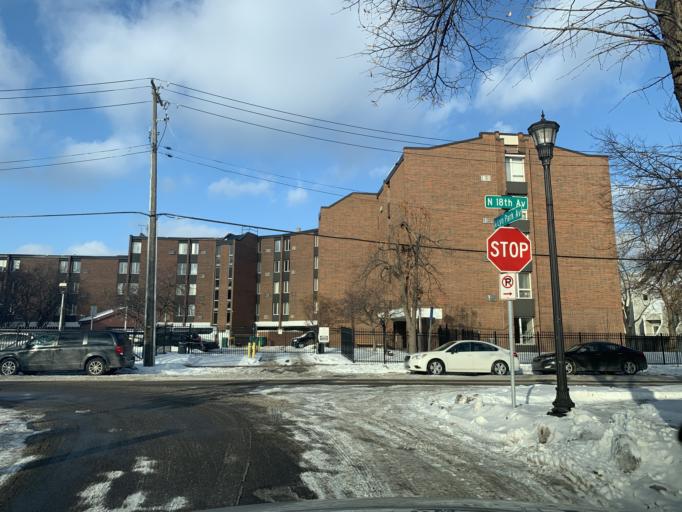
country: US
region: Minnesota
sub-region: Hennepin County
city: Minneapolis
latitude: 44.9973
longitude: -93.2862
